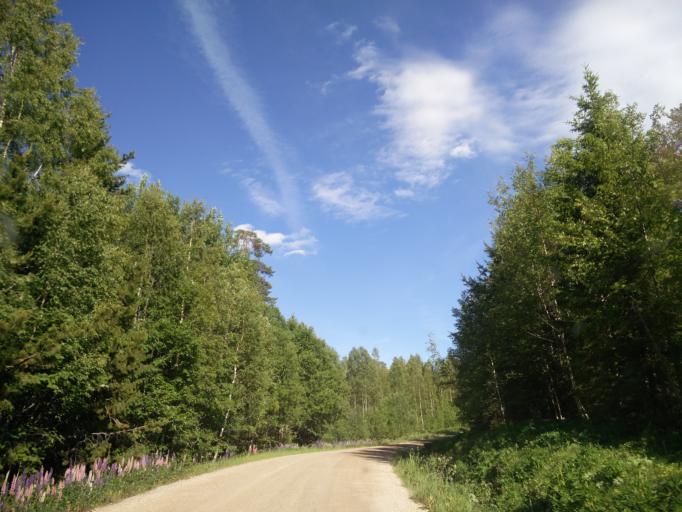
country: SE
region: Gaevleborg
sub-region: Hudiksvalls Kommun
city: Delsbo
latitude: 62.1861
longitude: 16.4677
